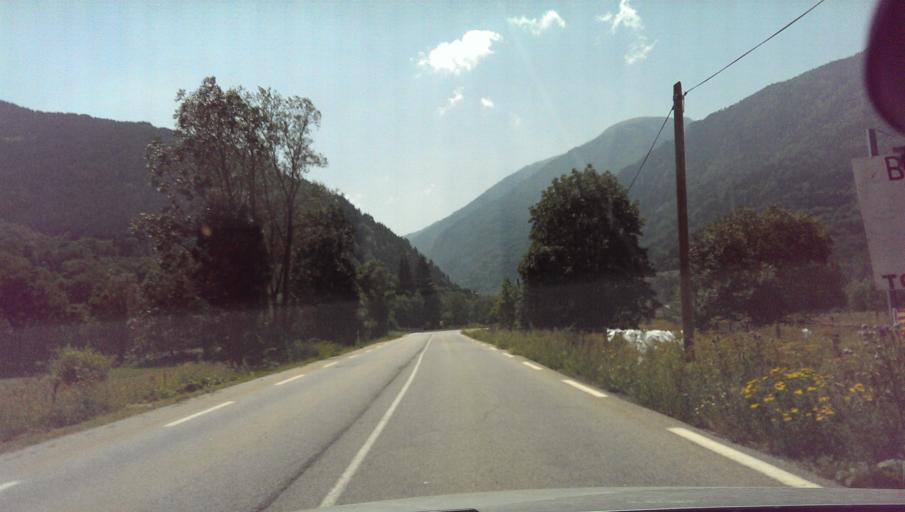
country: ES
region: Catalonia
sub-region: Provincia de Girona
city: Meranges
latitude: 42.5240
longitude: 1.8227
